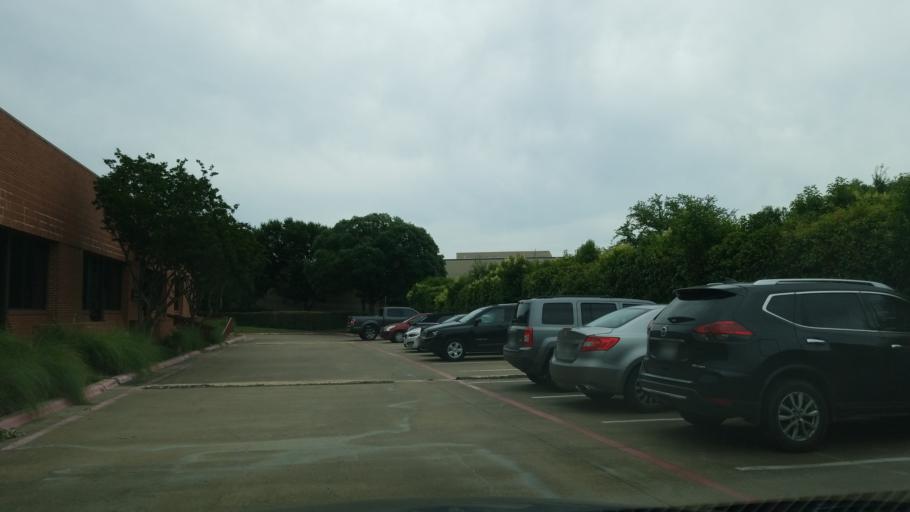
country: US
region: Texas
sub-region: Dallas County
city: Coppell
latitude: 32.8926
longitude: -96.9901
